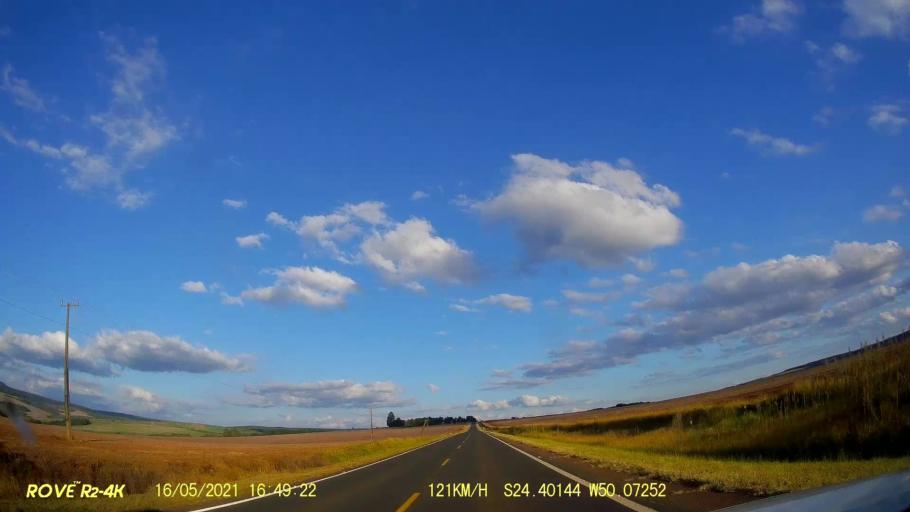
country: BR
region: Parana
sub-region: Pirai Do Sul
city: Pirai do Sul
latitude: -24.4018
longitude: -50.0722
